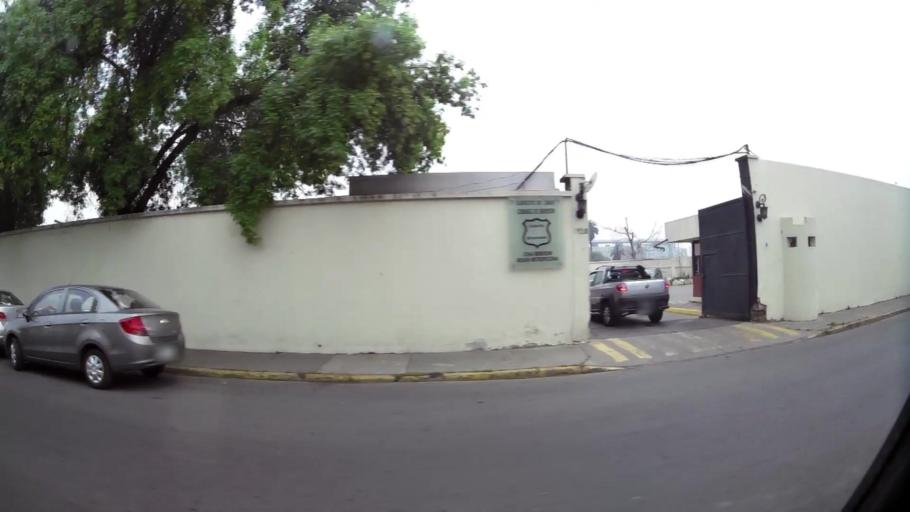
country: CL
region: Santiago Metropolitan
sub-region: Provincia de Santiago
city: Santiago
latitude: -33.4722
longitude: -70.6633
